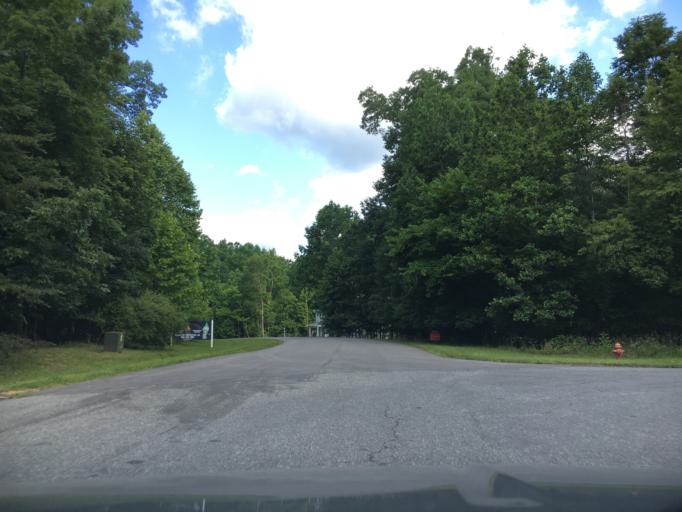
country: US
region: Virginia
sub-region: Bedford County
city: Forest
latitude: 37.3859
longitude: -79.2622
